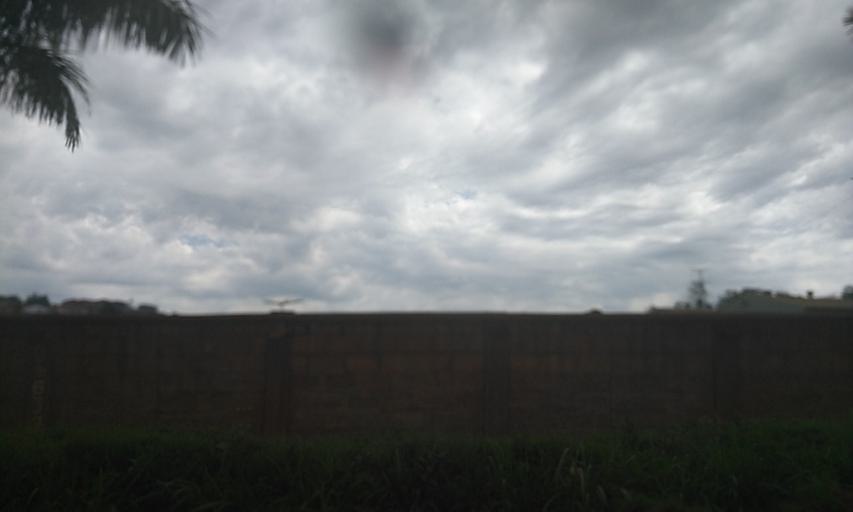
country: UG
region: Central Region
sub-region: Wakiso District
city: Kireka
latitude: 0.4076
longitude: 32.6299
